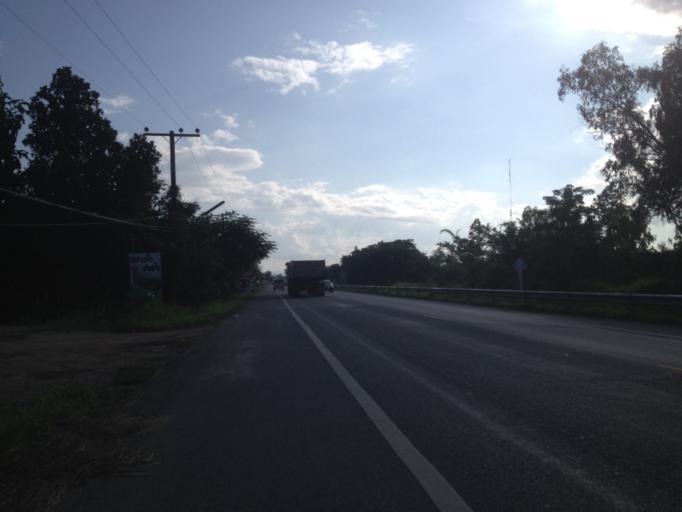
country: TH
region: Chiang Mai
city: San Pa Tong
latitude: 18.6573
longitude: 98.8659
